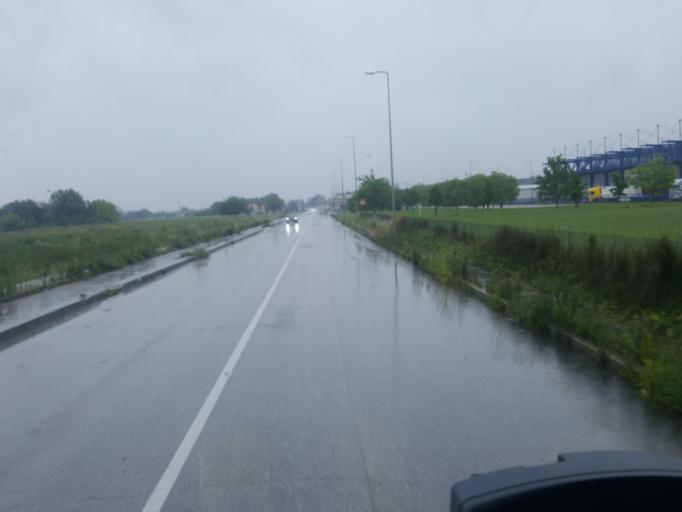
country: IT
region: Emilia-Romagna
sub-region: Forli-Cesena
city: Forli
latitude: 44.2410
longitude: 12.0864
